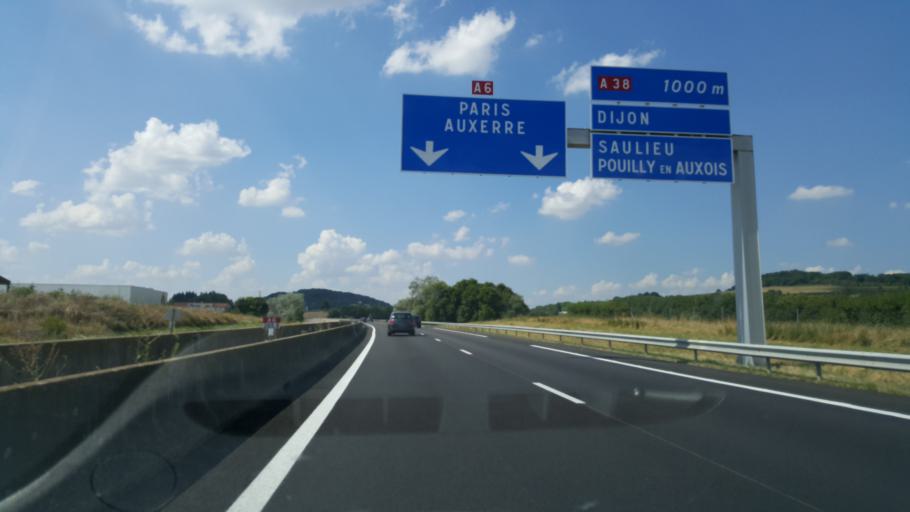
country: FR
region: Bourgogne
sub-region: Departement de la Cote-d'Or
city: Pouilly-en-Auxois
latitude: 47.2460
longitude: 4.5731
